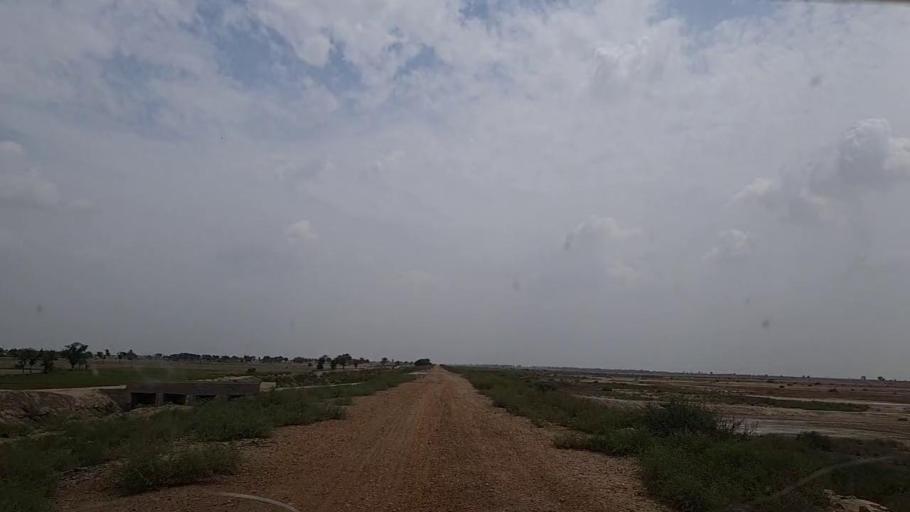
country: PK
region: Sindh
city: Johi
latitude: 26.7859
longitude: 67.5992
